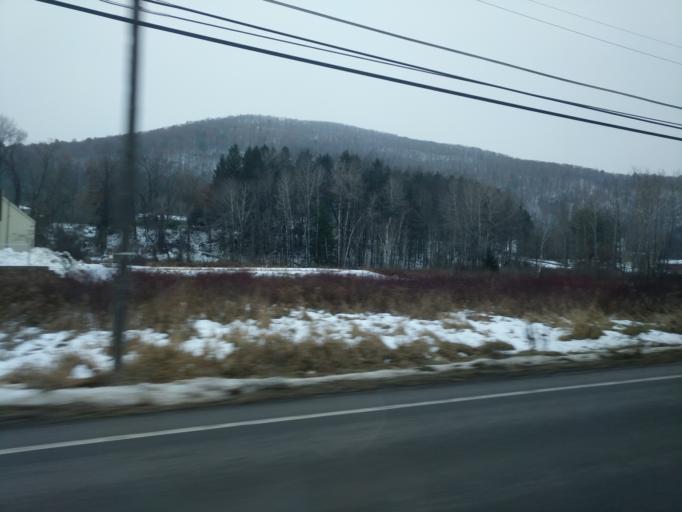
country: US
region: Pennsylvania
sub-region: Tioga County
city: Wellsboro
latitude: 41.8328
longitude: -77.2844
